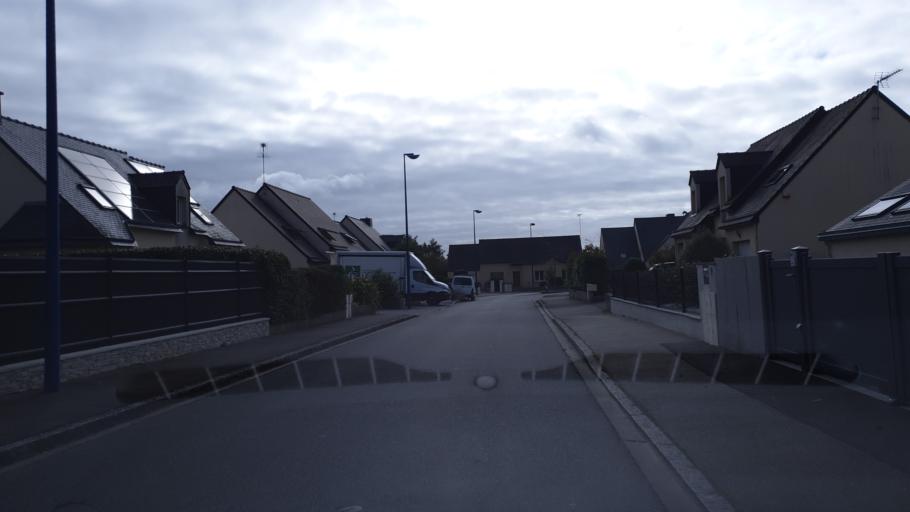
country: FR
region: Brittany
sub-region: Departement d'Ille-et-Vilaine
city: Janze
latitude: 47.9514
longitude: -1.4913
